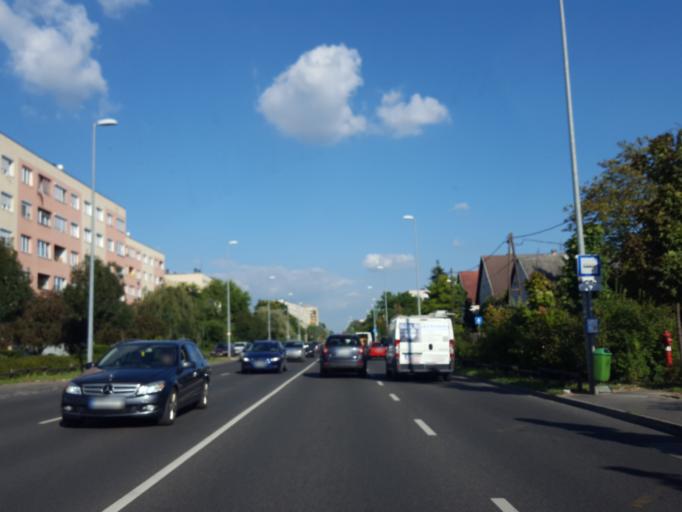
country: HU
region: Budapest
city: Budapest XI. keruelet
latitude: 47.4570
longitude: 19.0303
